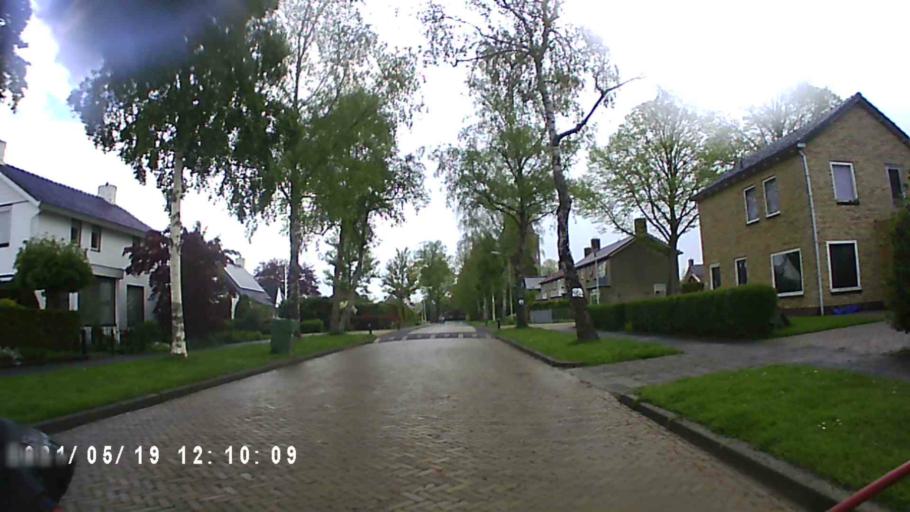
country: NL
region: Friesland
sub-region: Gemeente Achtkarspelen
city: Buitenpost
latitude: 53.2509
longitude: 6.1425
